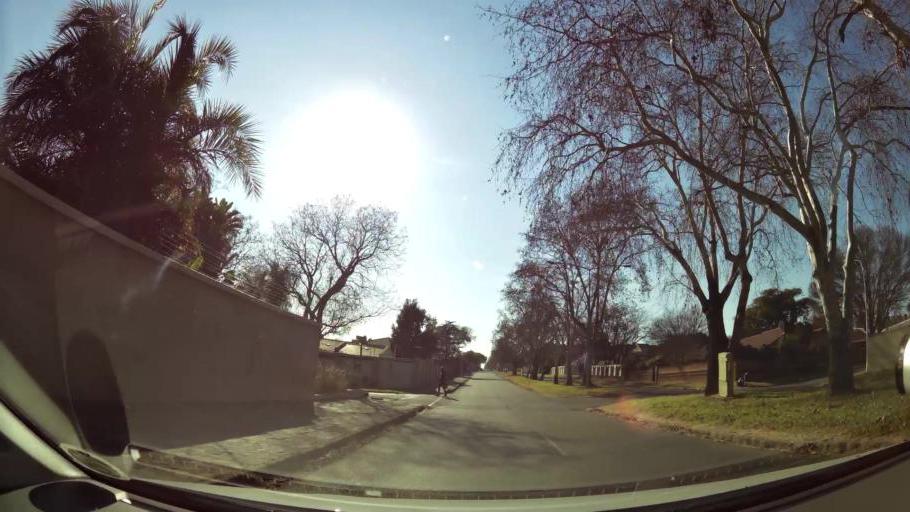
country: ZA
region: Gauteng
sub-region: City of Johannesburg Metropolitan Municipality
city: Modderfontein
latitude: -26.1422
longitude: 28.1499
